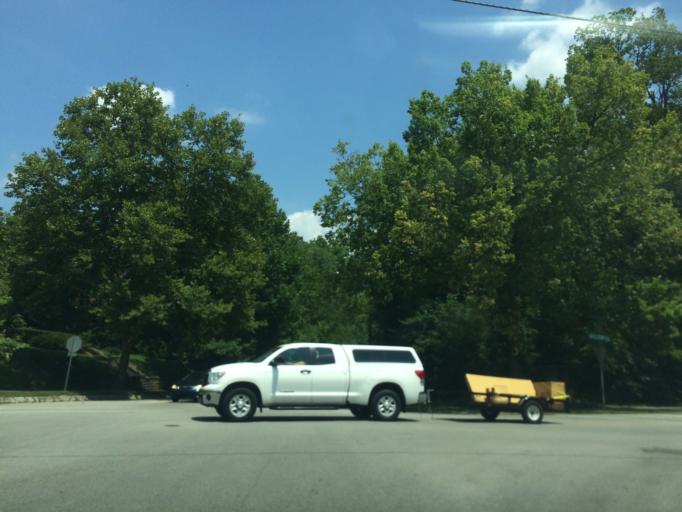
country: US
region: Kentucky
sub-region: Jefferson County
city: Audubon Park
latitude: 38.2366
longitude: -85.7097
